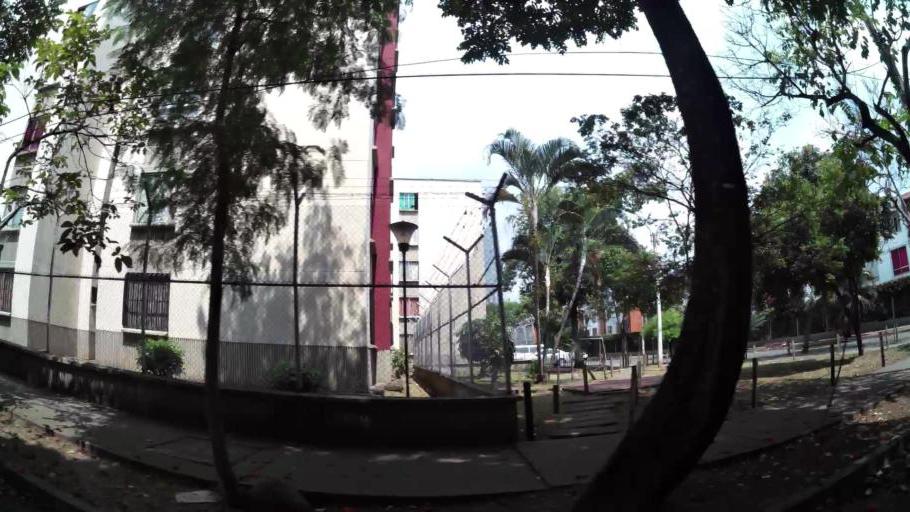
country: CO
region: Valle del Cauca
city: Cali
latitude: 3.4768
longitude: -76.5016
